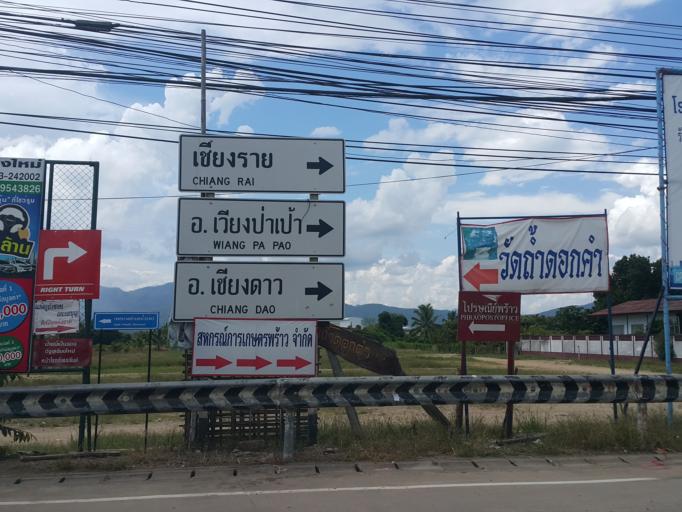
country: TH
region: Chiang Mai
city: Phrao
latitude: 19.3654
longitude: 99.2007
